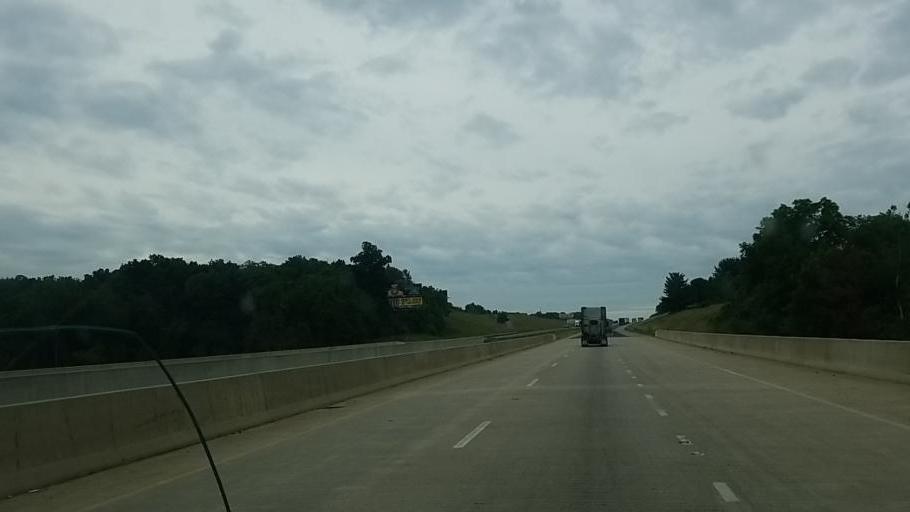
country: US
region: Indiana
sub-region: Steuben County
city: Angola
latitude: 41.7002
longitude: -85.0045
